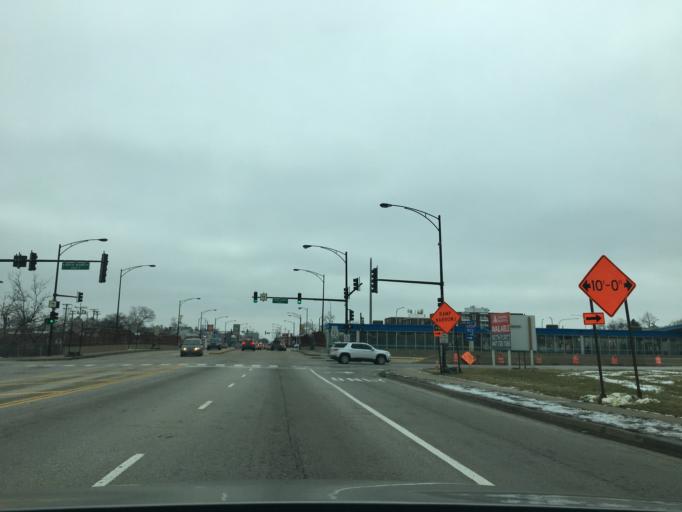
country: US
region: Illinois
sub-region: Cook County
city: Harwood Heights
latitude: 41.9833
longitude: -87.8070
